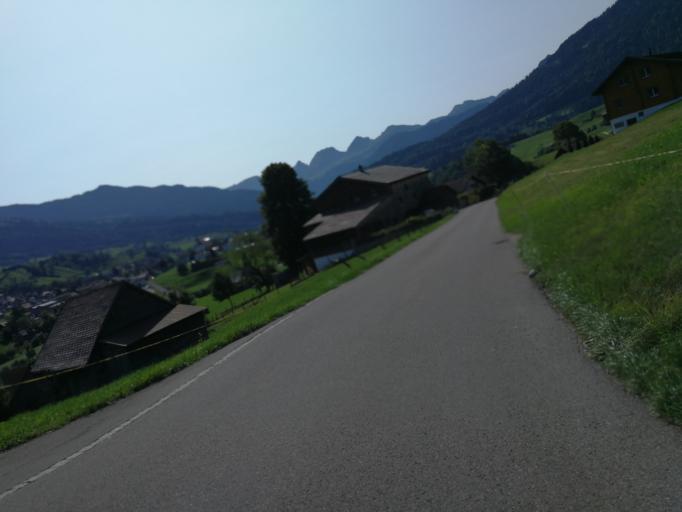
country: CH
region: Saint Gallen
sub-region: Wahlkreis Toggenburg
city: Krummenau
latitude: 47.2350
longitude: 9.1817
